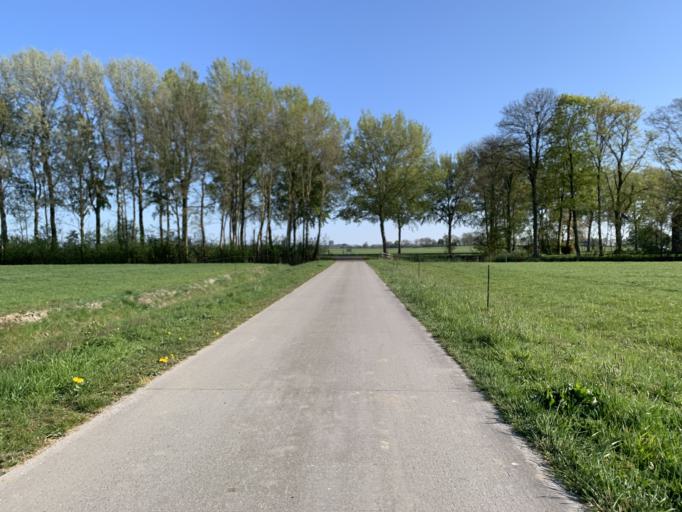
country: NL
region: Groningen
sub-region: Gemeente Winsum
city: Winsum
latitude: 53.2754
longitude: 6.5120
